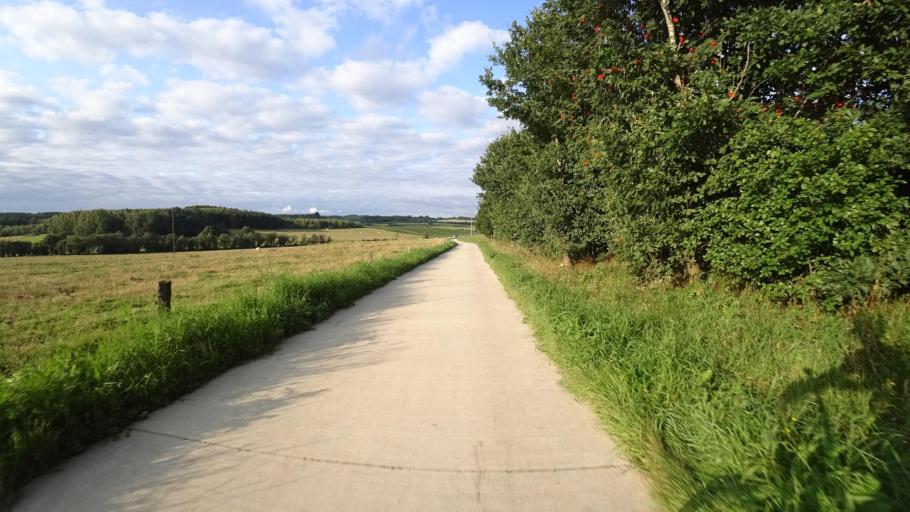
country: BE
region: Wallonia
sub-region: Province du Luxembourg
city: Neufchateau
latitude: 49.8486
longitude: 5.3499
